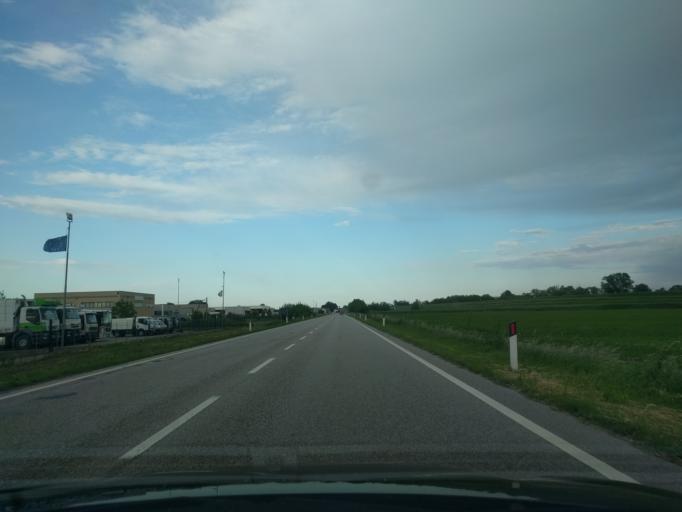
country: IT
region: Veneto
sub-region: Provincia di Rovigo
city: Canaro
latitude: 44.9263
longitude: 11.6954
